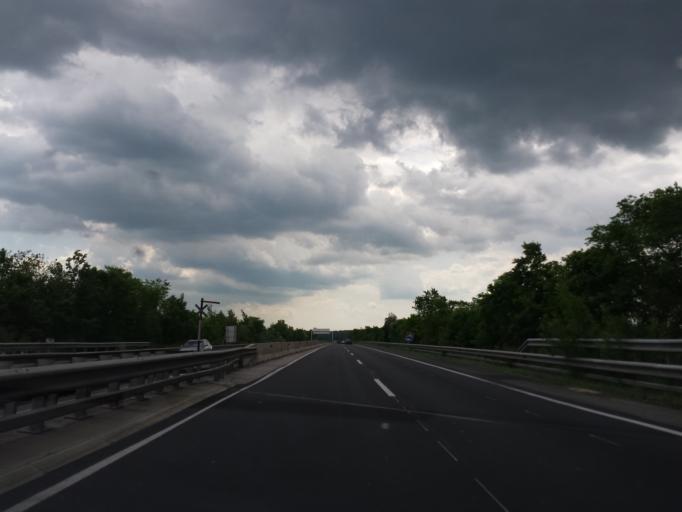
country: AT
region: Lower Austria
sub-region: Politischer Bezirk Wien-Umgebung
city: Fischamend Dorf
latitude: 48.1085
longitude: 16.6400
